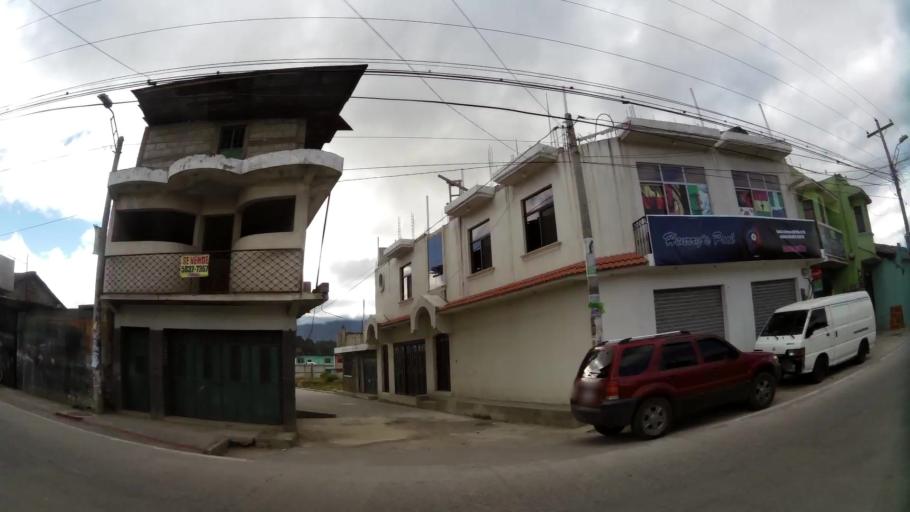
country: GT
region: Quetzaltenango
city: Salcaja
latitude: 14.8756
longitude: -91.4628
